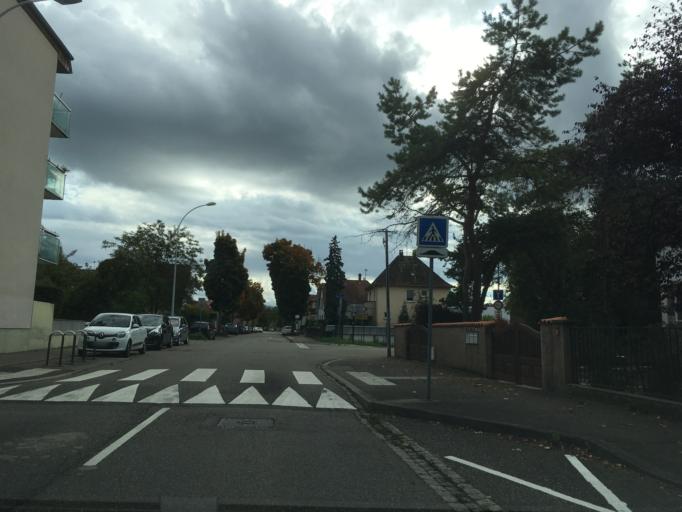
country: FR
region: Alsace
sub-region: Departement du Bas-Rhin
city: Illkirch-Graffenstaden
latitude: 48.5389
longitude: 7.7610
